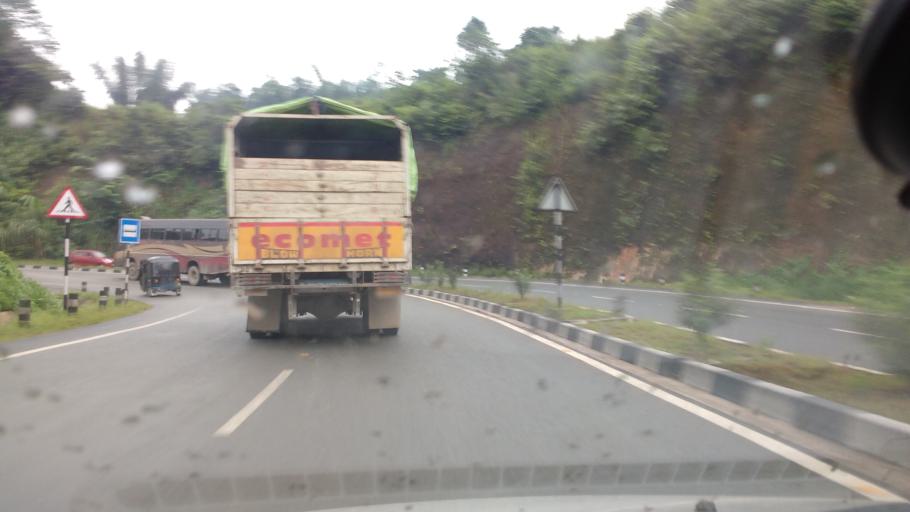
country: IN
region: Meghalaya
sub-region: Ri-Bhoi
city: Nongpoh
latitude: 25.8188
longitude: 91.8713
